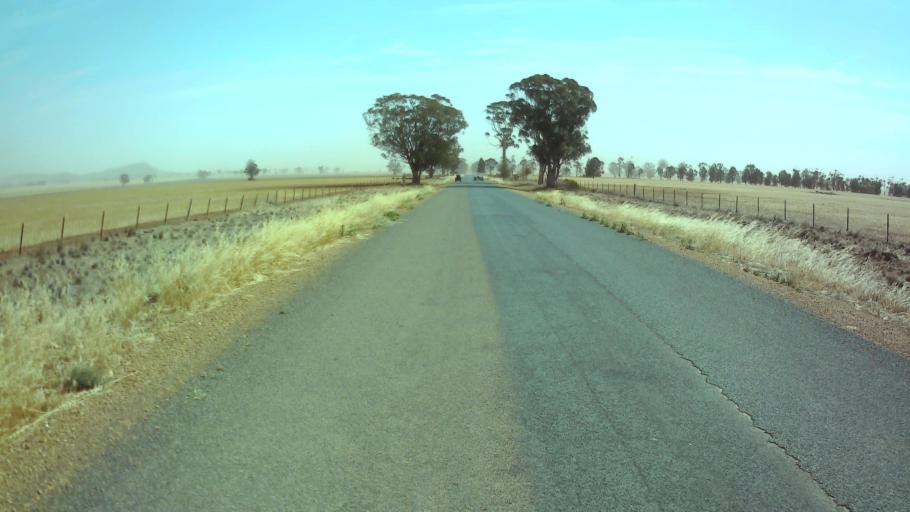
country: AU
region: New South Wales
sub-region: Weddin
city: Grenfell
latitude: -33.7705
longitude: 147.9869
